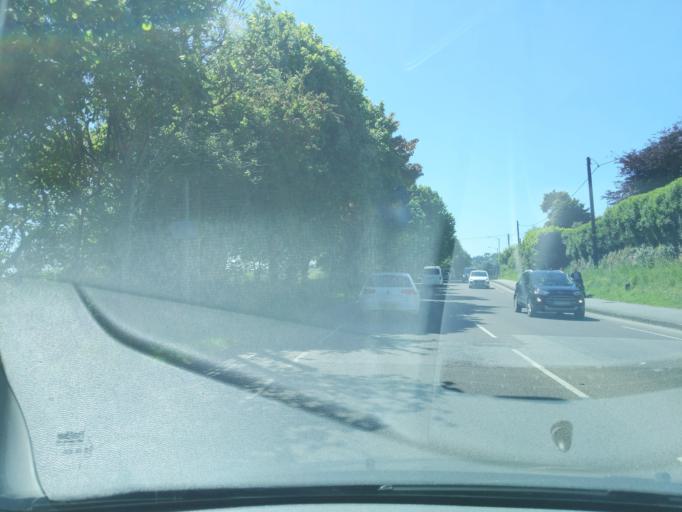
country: GB
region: England
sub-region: Cornwall
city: St Austell
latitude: 50.3341
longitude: -4.7797
